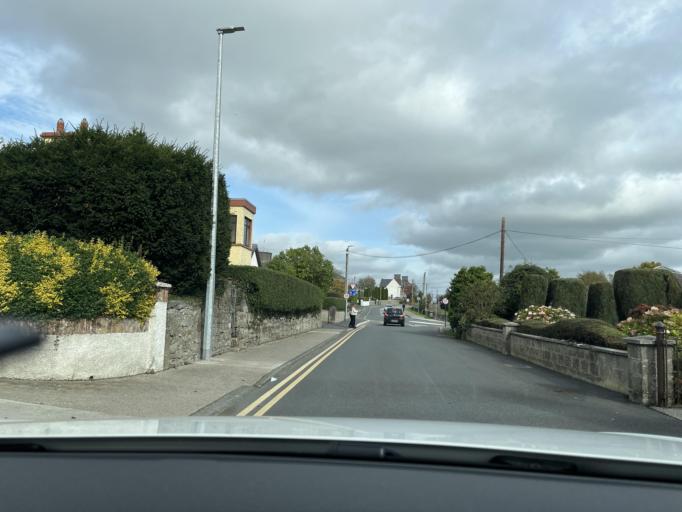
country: IE
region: Connaught
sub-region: County Leitrim
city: Carrick-on-Shannon
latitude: 53.9486
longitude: -8.0879
